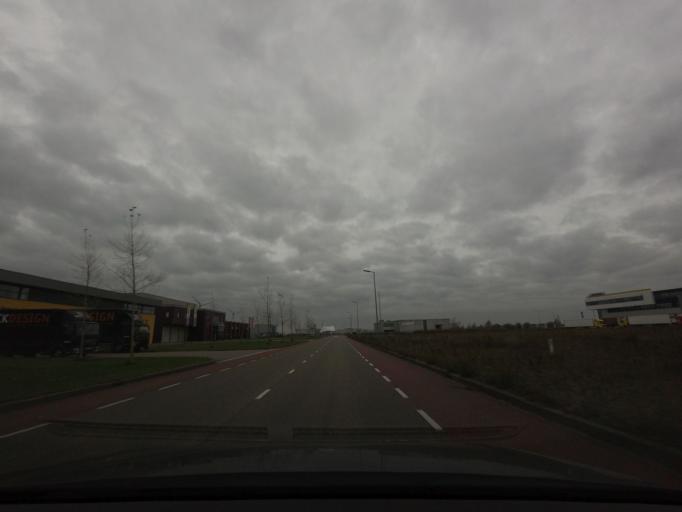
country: NL
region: North Holland
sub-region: Gemeente Alkmaar
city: Alkmaar
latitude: 52.6037
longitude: 4.7532
